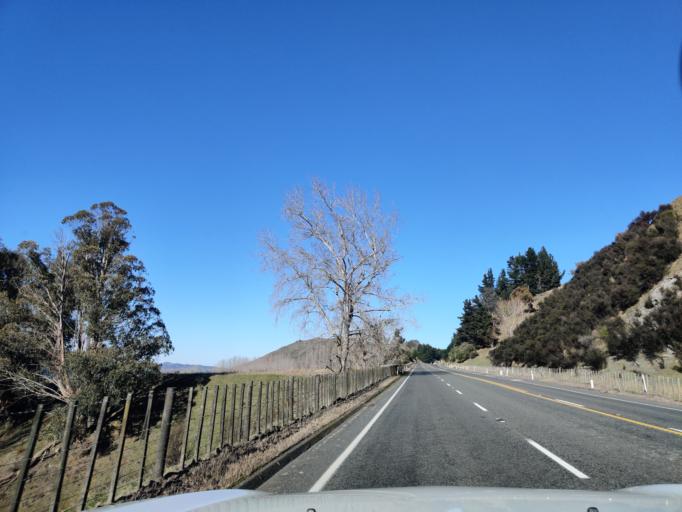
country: NZ
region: Manawatu-Wanganui
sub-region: Ruapehu District
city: Waiouru
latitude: -39.7644
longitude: 175.8022
